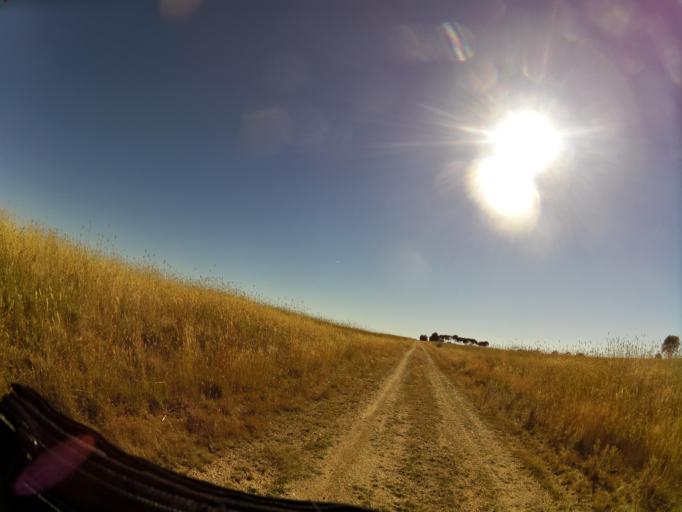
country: AU
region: Victoria
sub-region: Ballarat North
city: Delacombe
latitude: -37.6883
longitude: 143.3876
